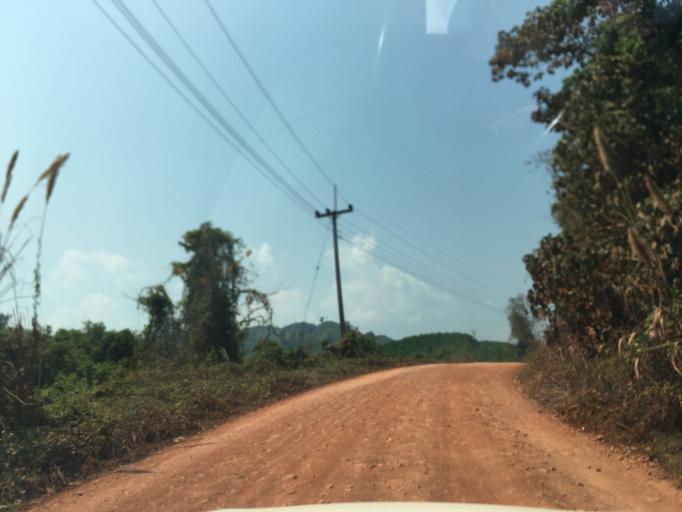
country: LA
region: Bolikhamxai
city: Bolikhan
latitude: 18.7299
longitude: 103.6354
